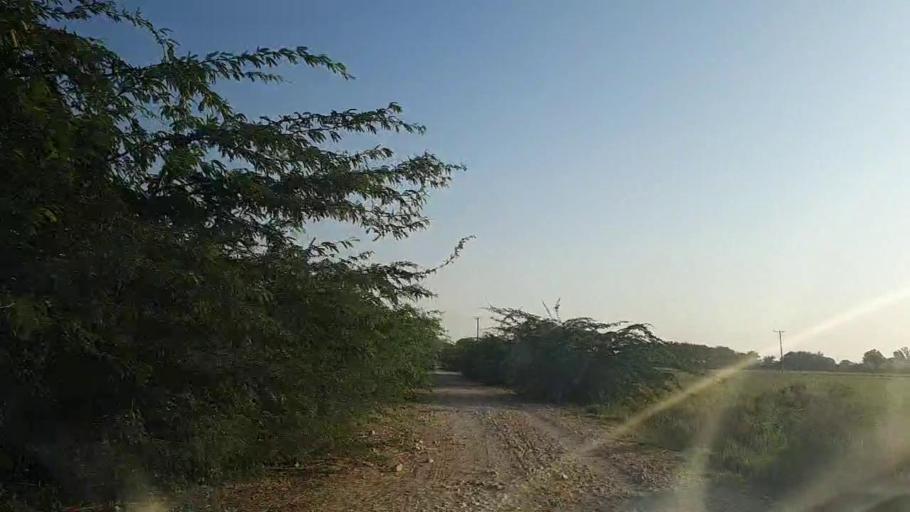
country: PK
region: Sindh
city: Jati
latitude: 24.4186
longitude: 68.1853
